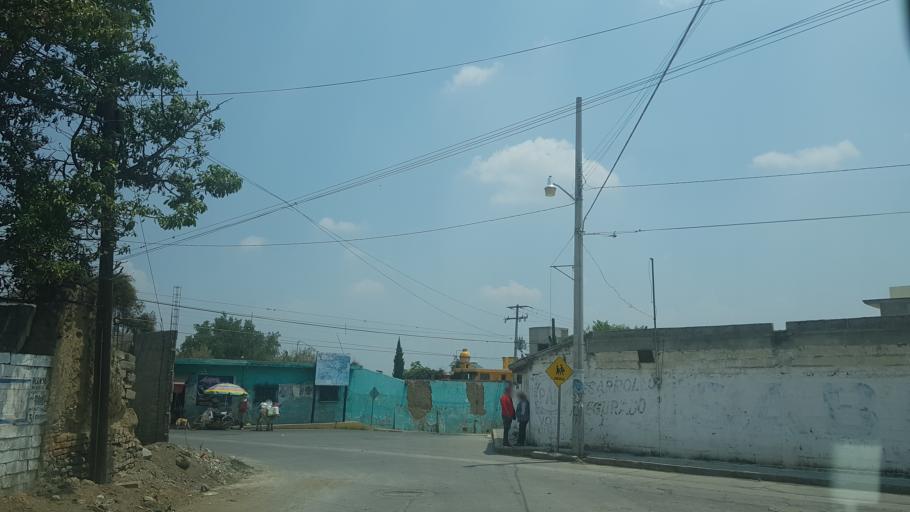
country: MX
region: Puebla
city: San Andres Calpan
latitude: 19.1056
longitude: -98.4661
